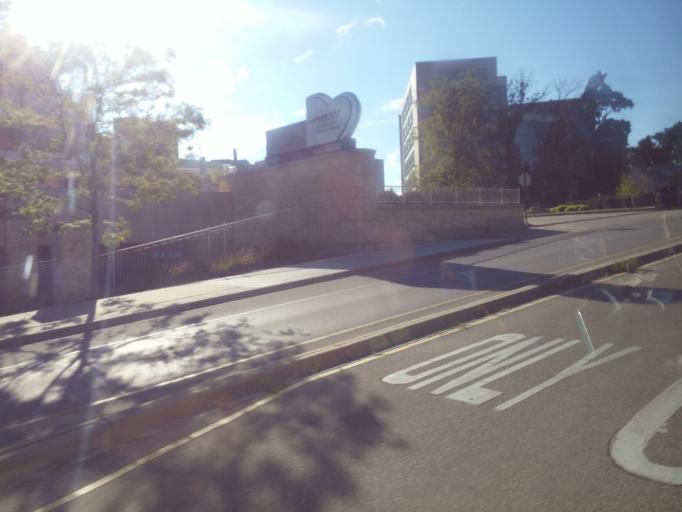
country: US
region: Wisconsin
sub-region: Dane County
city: Shorewood Hills
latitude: 43.0765
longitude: -89.4340
